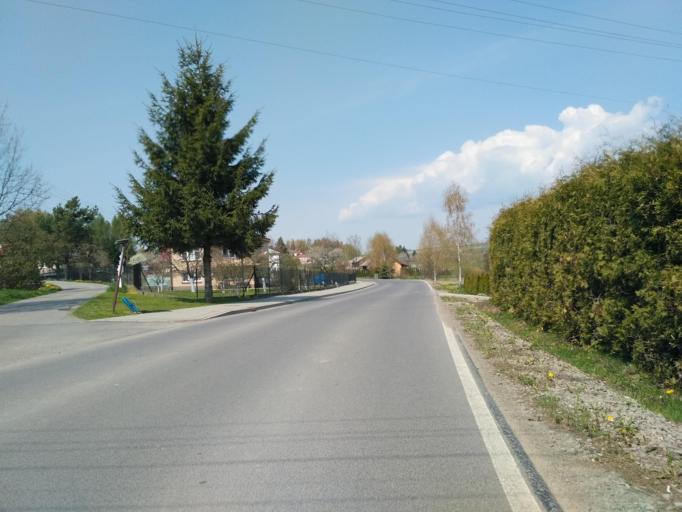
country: PL
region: Subcarpathian Voivodeship
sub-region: Powiat krosnienski
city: Chorkowka
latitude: 49.6523
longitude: 21.6709
